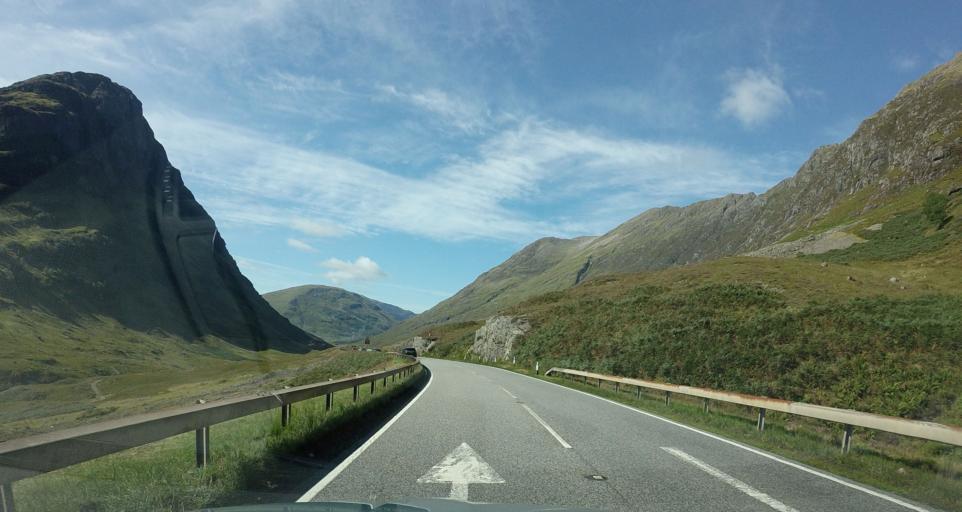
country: GB
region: Scotland
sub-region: Highland
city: Fort William
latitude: 56.6669
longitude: -4.9918
